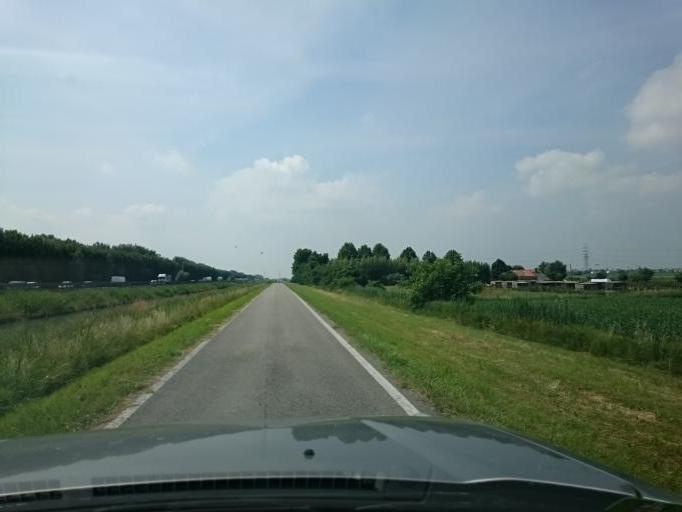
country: IT
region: Veneto
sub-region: Provincia di Padova
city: Codevigo
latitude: 45.2828
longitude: 12.1292
